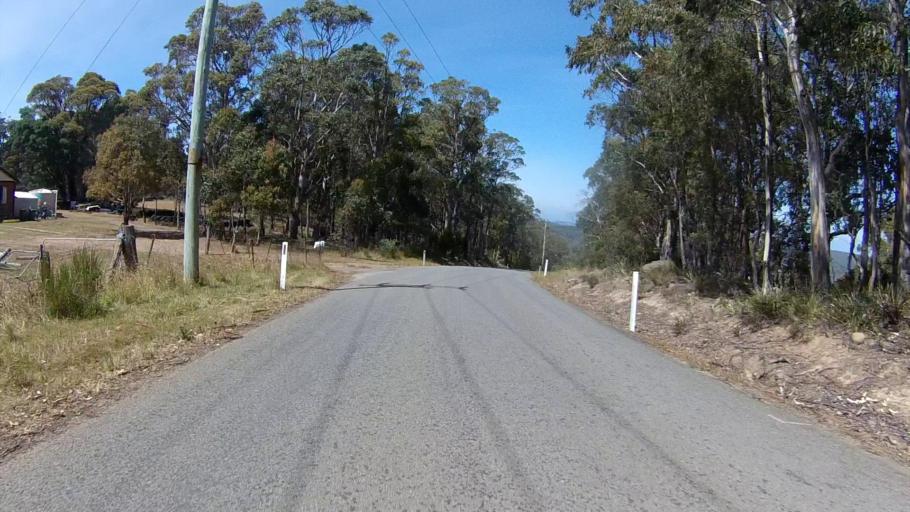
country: AU
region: Tasmania
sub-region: Sorell
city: Sorell
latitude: -42.7360
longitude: 147.7383
